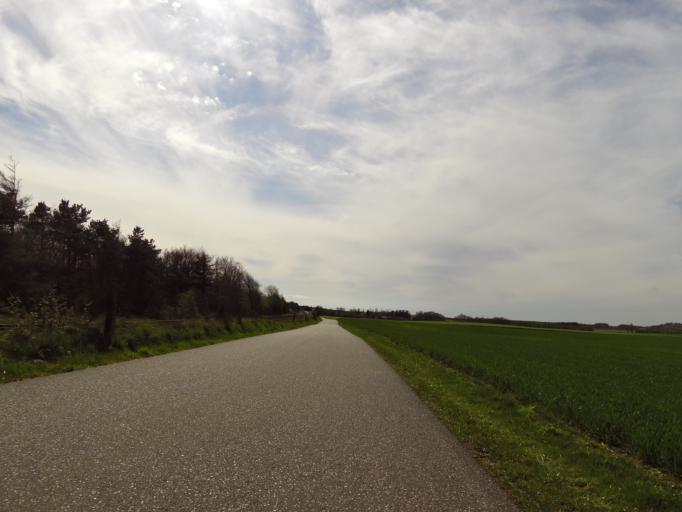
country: DK
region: Central Jutland
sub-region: Skive Kommune
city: Skive
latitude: 56.5626
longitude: 8.9806
